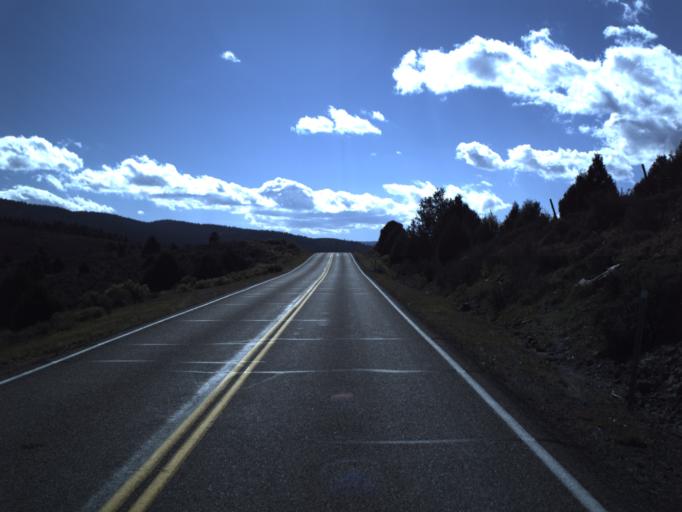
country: US
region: Utah
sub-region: Garfield County
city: Panguitch
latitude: 37.7653
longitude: -112.5529
